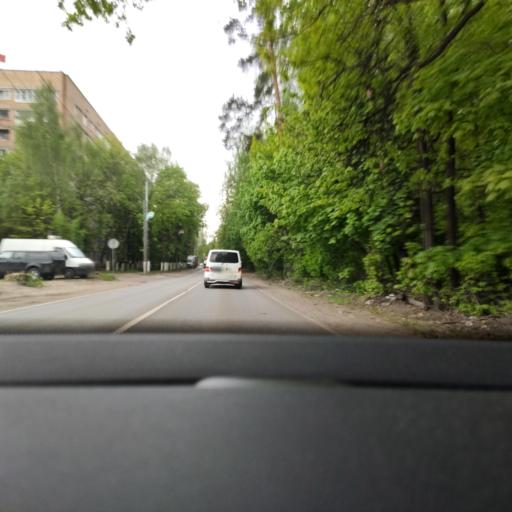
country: RU
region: Moskovskaya
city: Saltykovka
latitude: 55.7334
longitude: 37.9676
